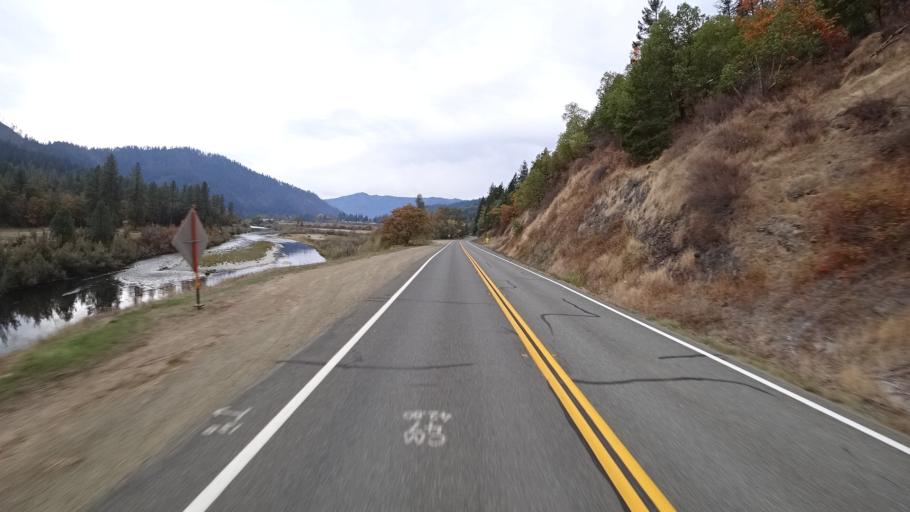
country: US
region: California
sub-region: Siskiyou County
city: Happy Camp
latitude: 41.8108
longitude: -123.3602
